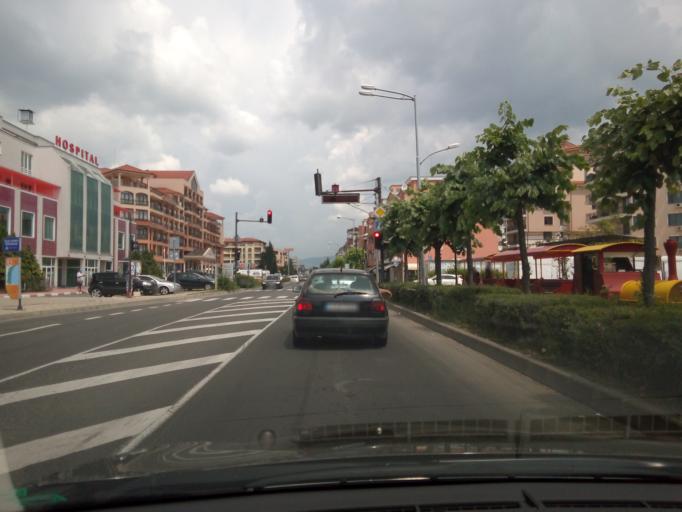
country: BG
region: Burgas
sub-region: Obshtina Nesebur
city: Nesebar
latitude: 42.6672
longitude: 27.7070
